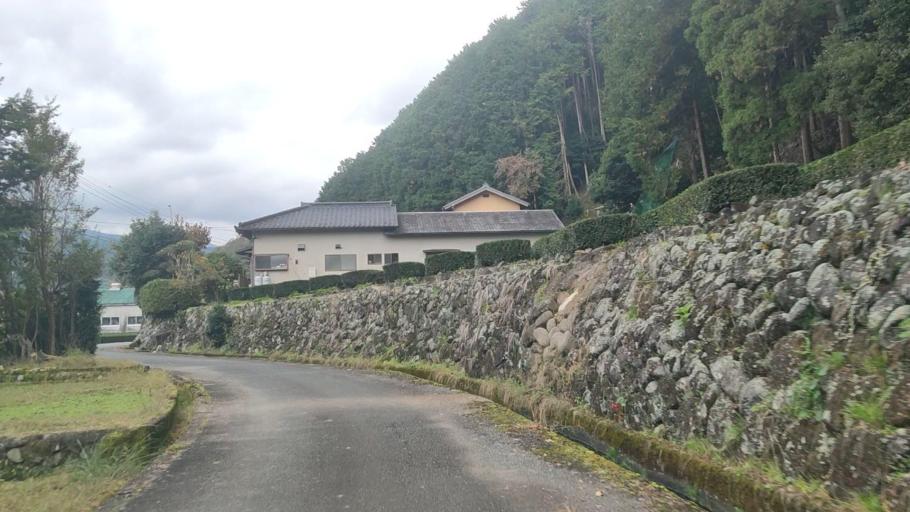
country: JP
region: Shizuoka
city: Ito
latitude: 34.9325
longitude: 138.9910
